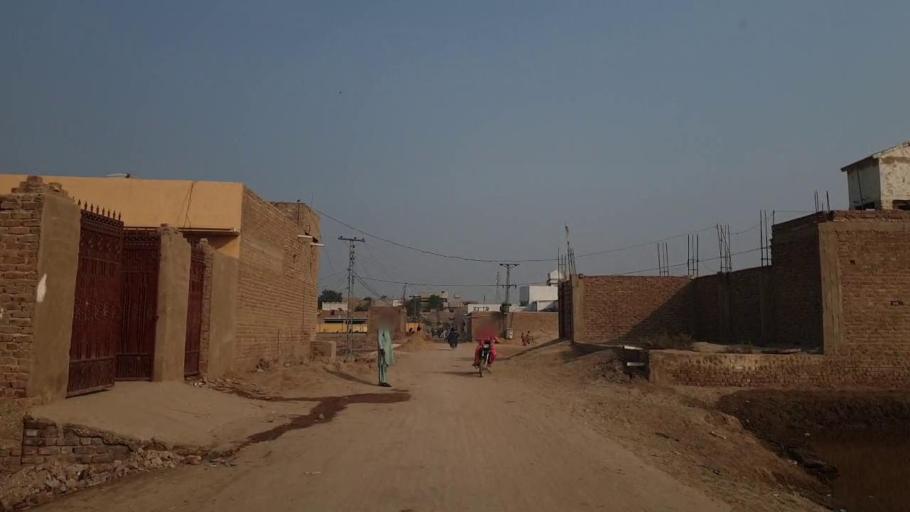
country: PK
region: Sindh
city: Bhan
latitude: 26.5561
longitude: 67.7154
